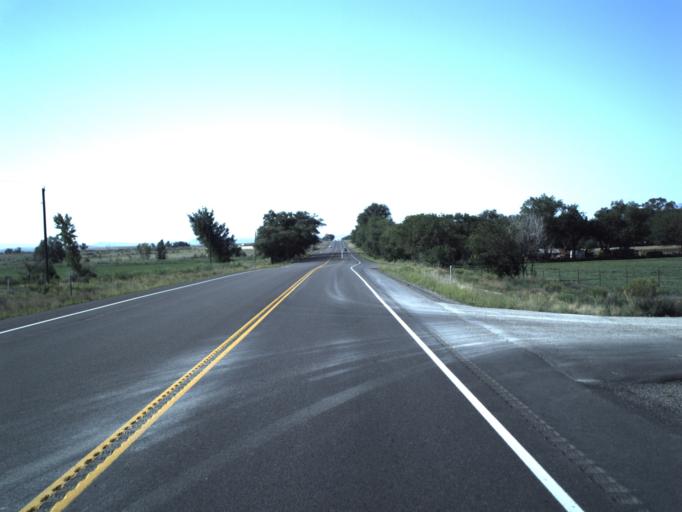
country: US
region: Utah
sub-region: Emery County
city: Castle Dale
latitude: 39.2591
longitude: -110.9833
